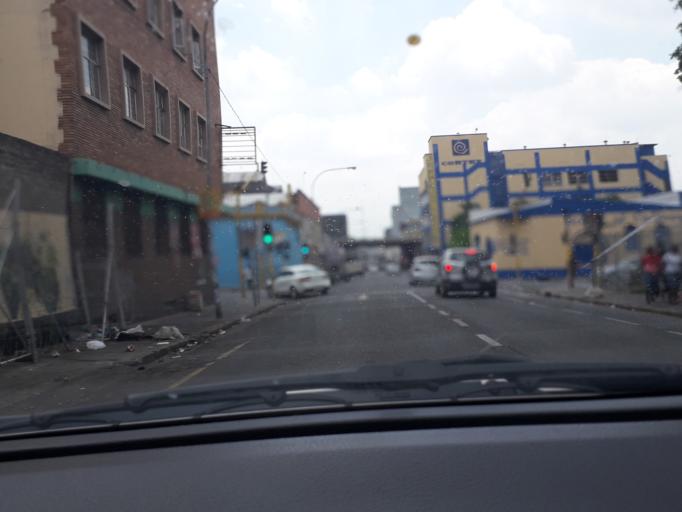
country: ZA
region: Gauteng
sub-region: City of Johannesburg Metropolitan Municipality
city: Johannesburg
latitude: -26.2064
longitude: 28.0525
